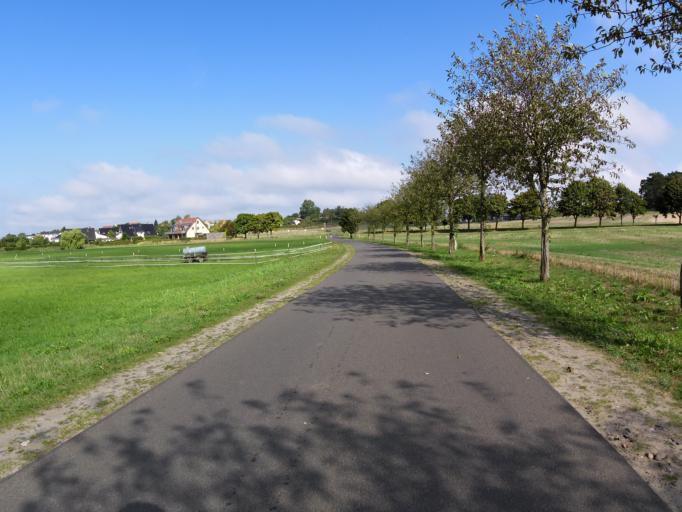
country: DE
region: Mecklenburg-Vorpommern
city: Loddin
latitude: 54.0069
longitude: 14.0470
